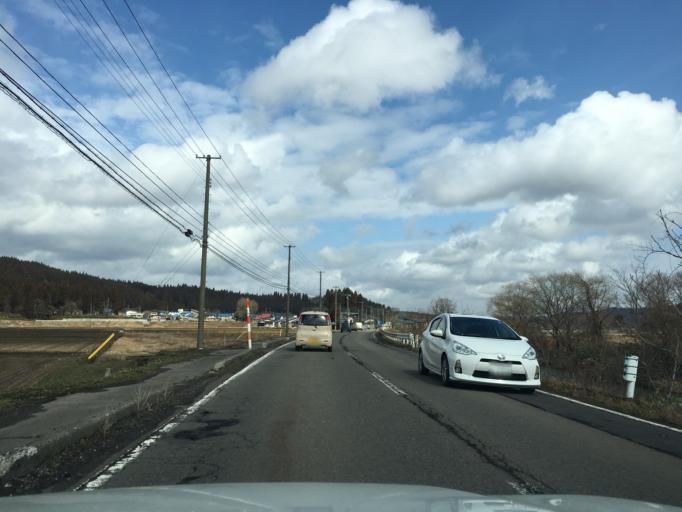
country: JP
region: Akita
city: Takanosu
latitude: 40.0397
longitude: 140.2793
